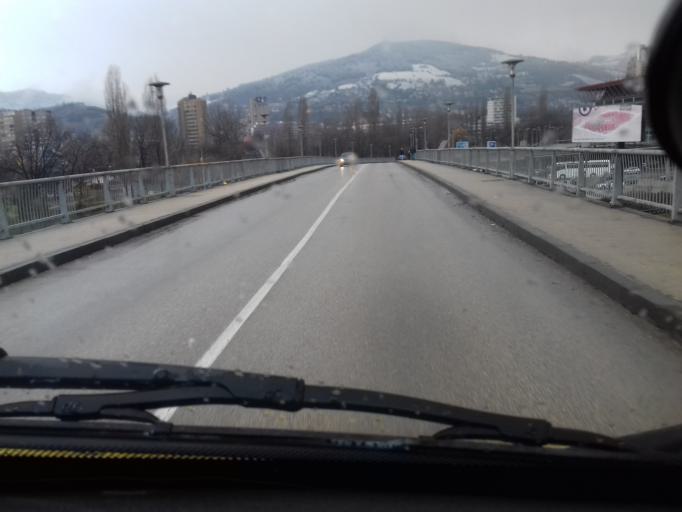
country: BA
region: Federation of Bosnia and Herzegovina
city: Zenica
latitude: 44.2018
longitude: 17.9158
